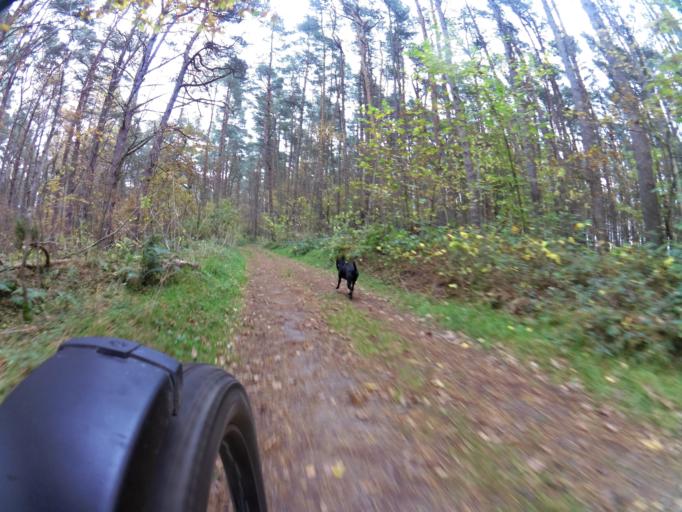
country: PL
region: Pomeranian Voivodeship
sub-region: Powiat pucki
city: Krokowa
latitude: 54.8296
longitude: 18.1228
